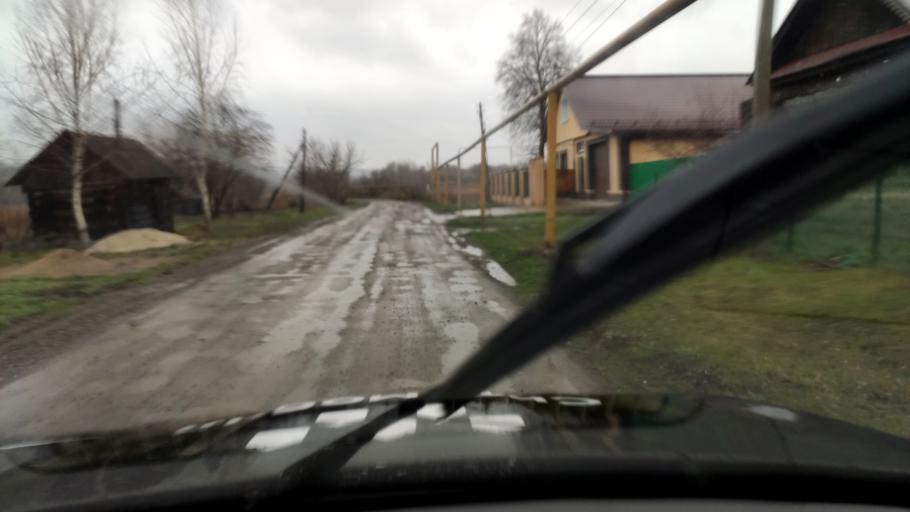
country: RU
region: Samara
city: Balasheyka
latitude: 53.2312
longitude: 48.2407
